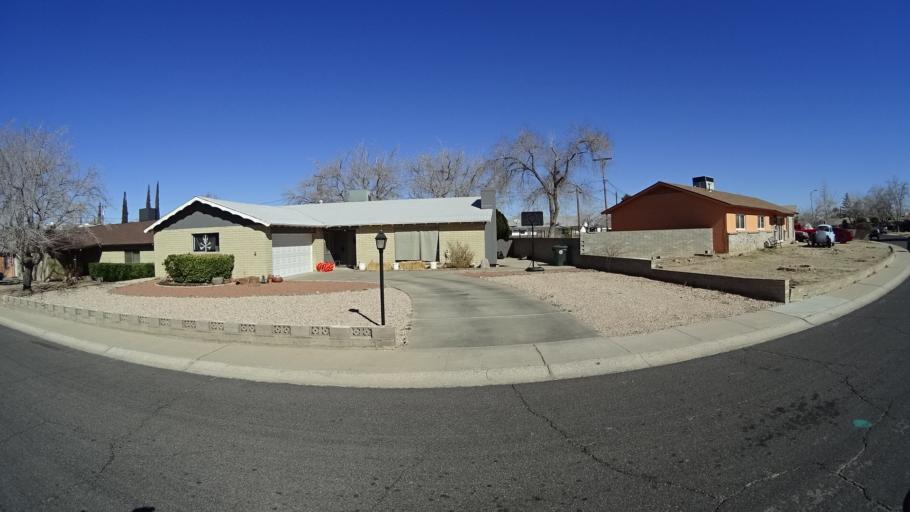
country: US
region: Arizona
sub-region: Mohave County
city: Kingman
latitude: 35.2118
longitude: -114.0200
